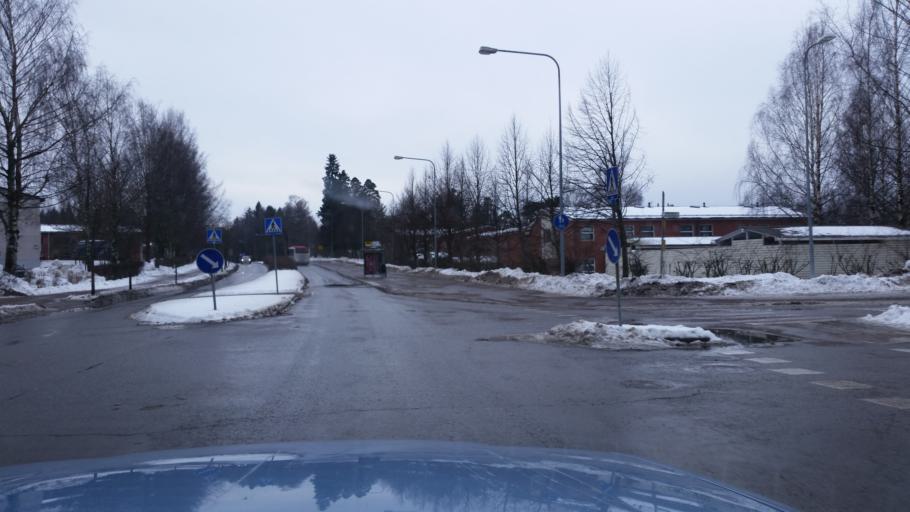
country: FI
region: Uusimaa
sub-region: Helsinki
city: Vantaa
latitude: 60.2671
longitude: 25.0585
